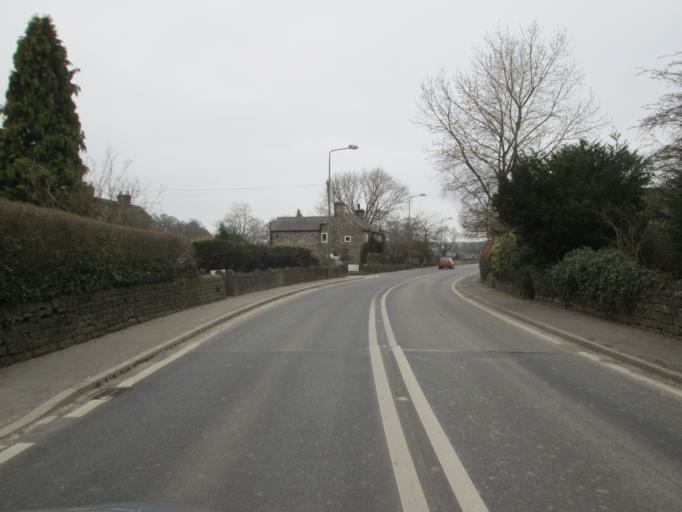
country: GB
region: England
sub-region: Derbyshire
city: Bakewell
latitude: 53.1888
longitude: -1.6188
